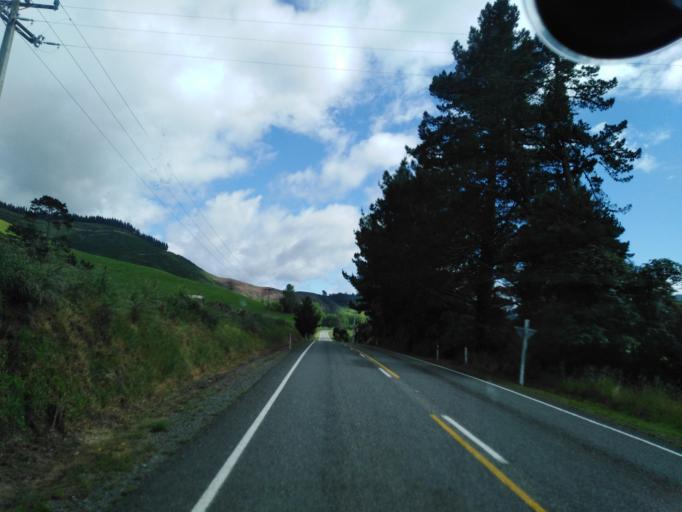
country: NZ
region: Nelson
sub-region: Nelson City
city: Nelson
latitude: -41.2735
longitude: 173.5729
